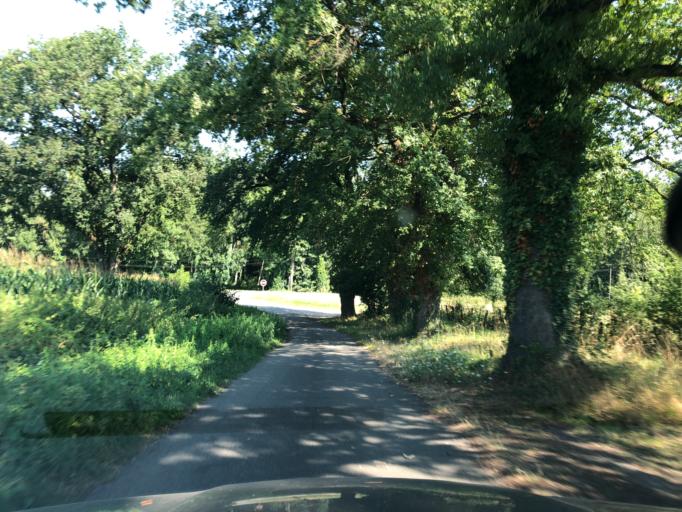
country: FR
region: Auvergne
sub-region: Departement de l'Allier
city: Cusset
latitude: 46.1360
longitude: 3.4774
